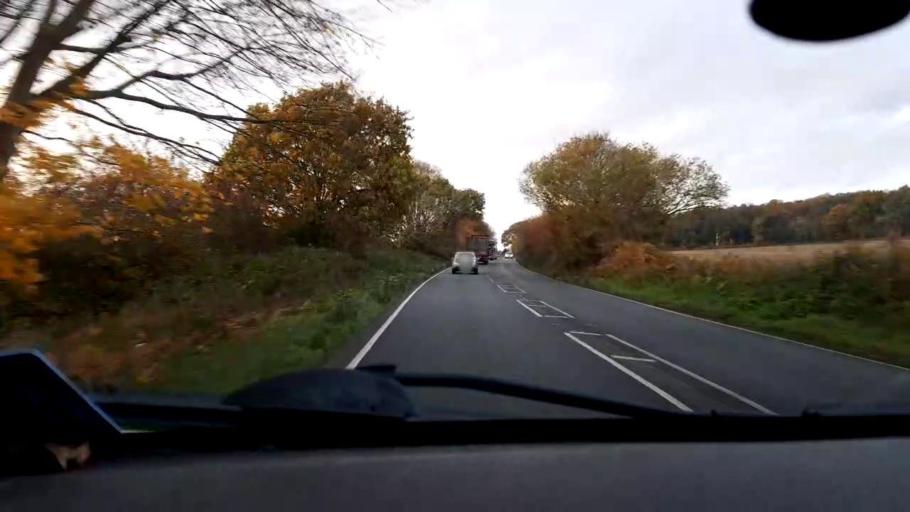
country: GB
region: England
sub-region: Norfolk
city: Costessey
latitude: 52.6994
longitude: 1.1616
